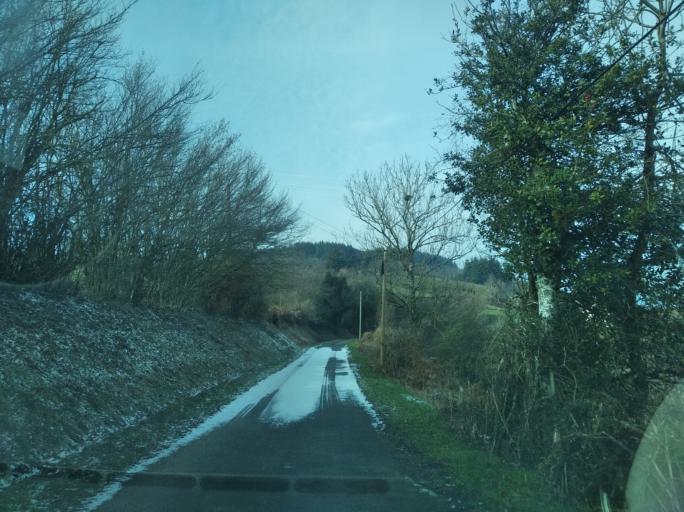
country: FR
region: Auvergne
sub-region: Departement de l'Allier
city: Le Mayet-de-Montagne
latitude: 46.1415
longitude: 3.7566
